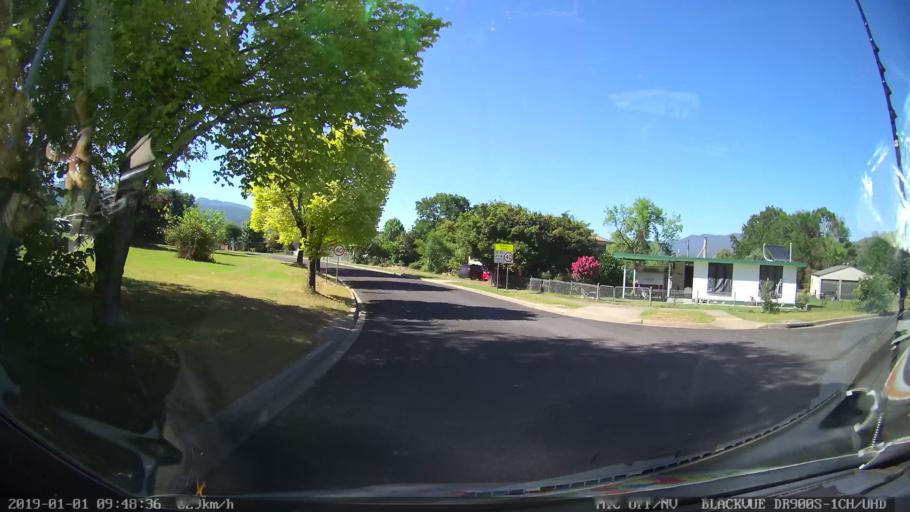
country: AU
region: New South Wales
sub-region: Snowy River
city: Jindabyne
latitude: -36.2123
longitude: 148.1318
